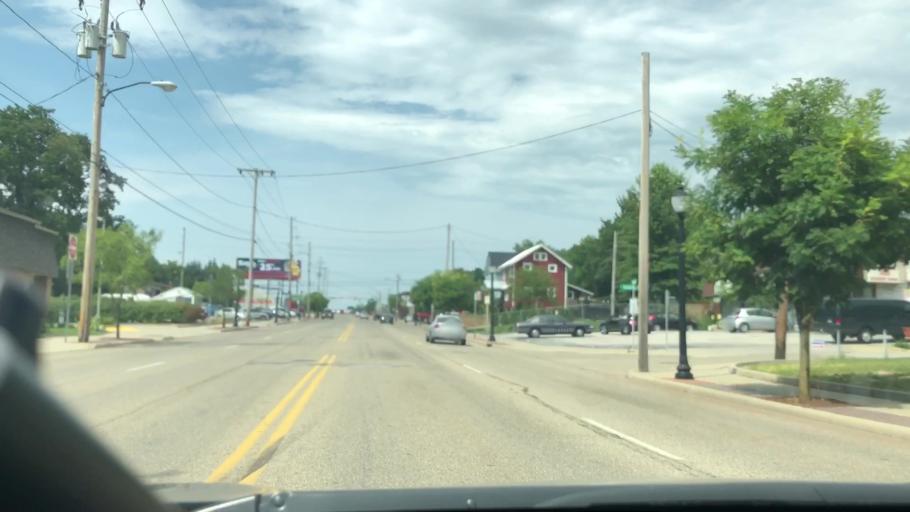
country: US
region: Ohio
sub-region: Summit County
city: Portage Lakes
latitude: 41.0372
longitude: -81.5269
